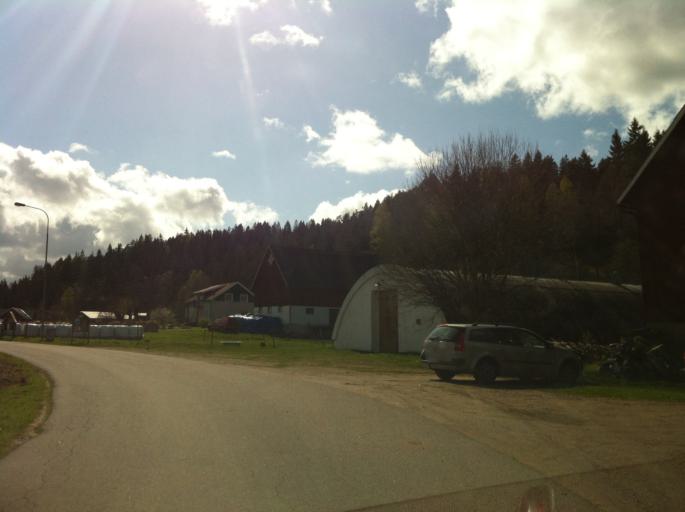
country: SE
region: Vaestra Goetaland
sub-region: Bollebygds Kommun
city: Bollebygd
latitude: 57.7906
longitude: 12.6155
